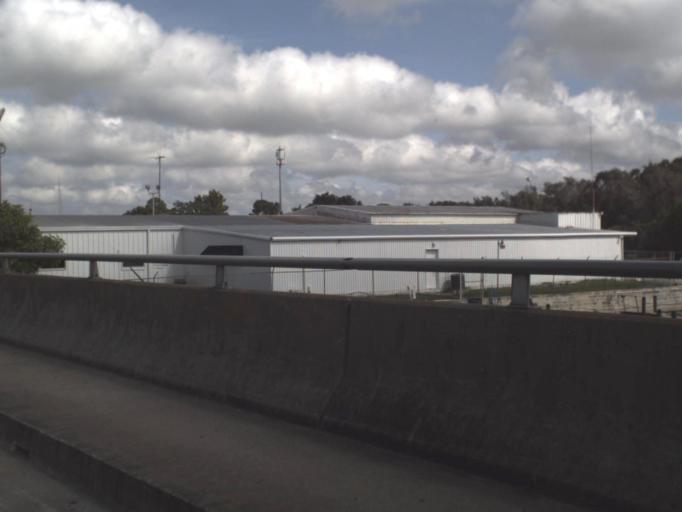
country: US
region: Florida
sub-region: Manatee County
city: Whitfield
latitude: 27.4162
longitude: -82.5744
